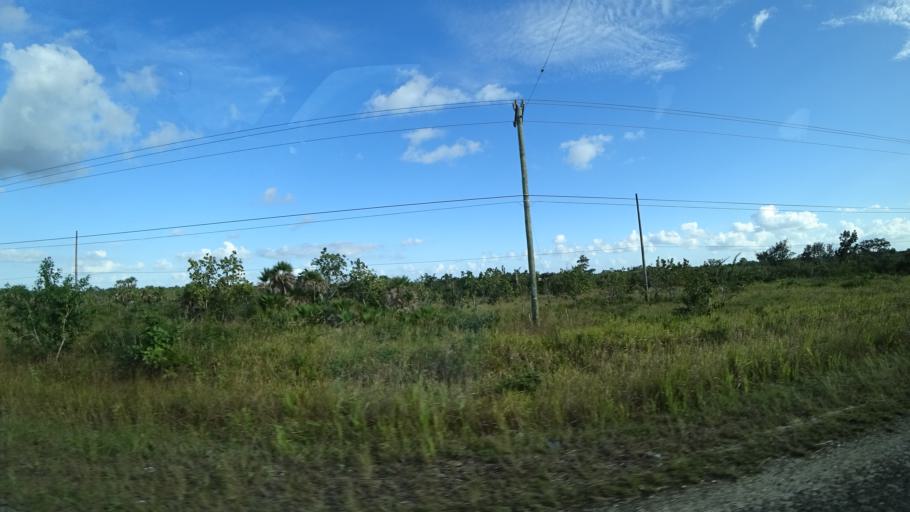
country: BZ
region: Belize
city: Belize City
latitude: 17.5791
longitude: -88.3823
